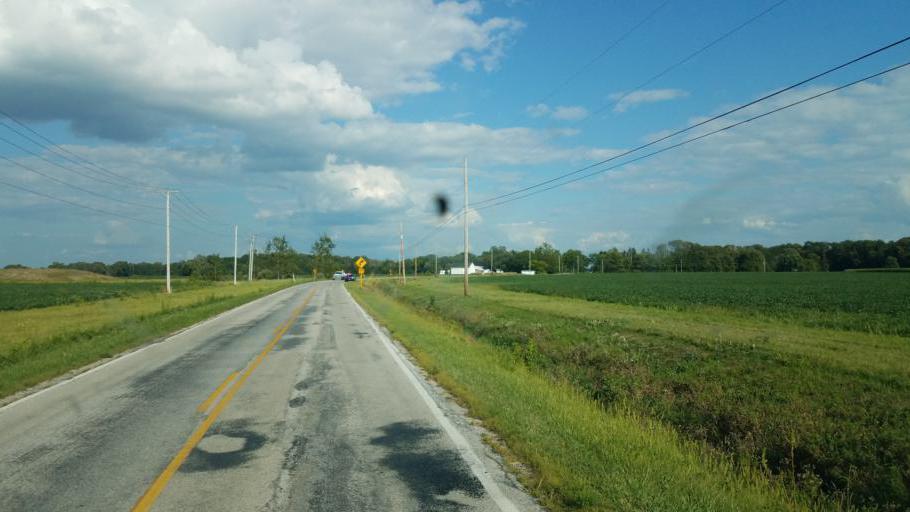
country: US
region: Ohio
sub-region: Wood County
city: Bowling Green
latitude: 41.3635
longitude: -83.6047
